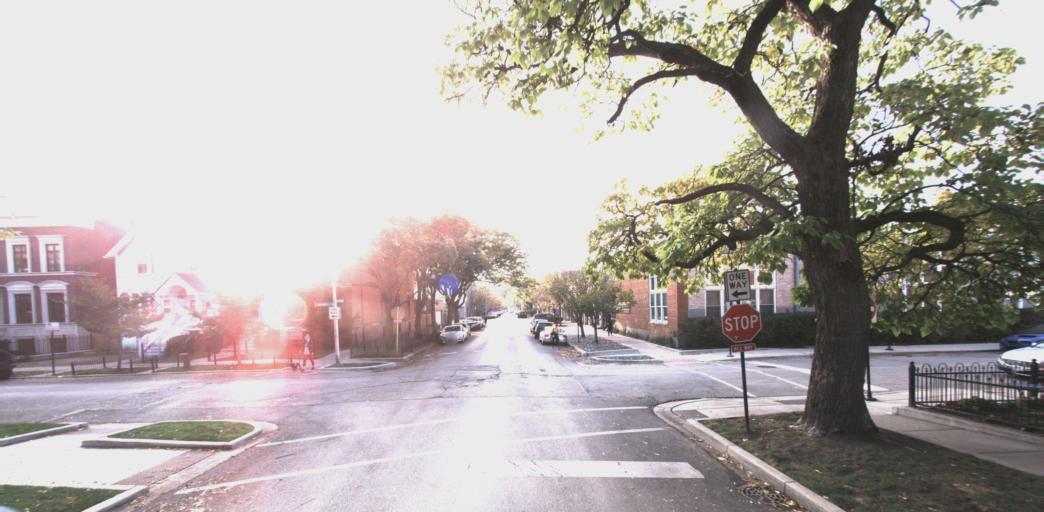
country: US
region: Illinois
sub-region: Cook County
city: Chicago
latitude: 41.9271
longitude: -87.6604
